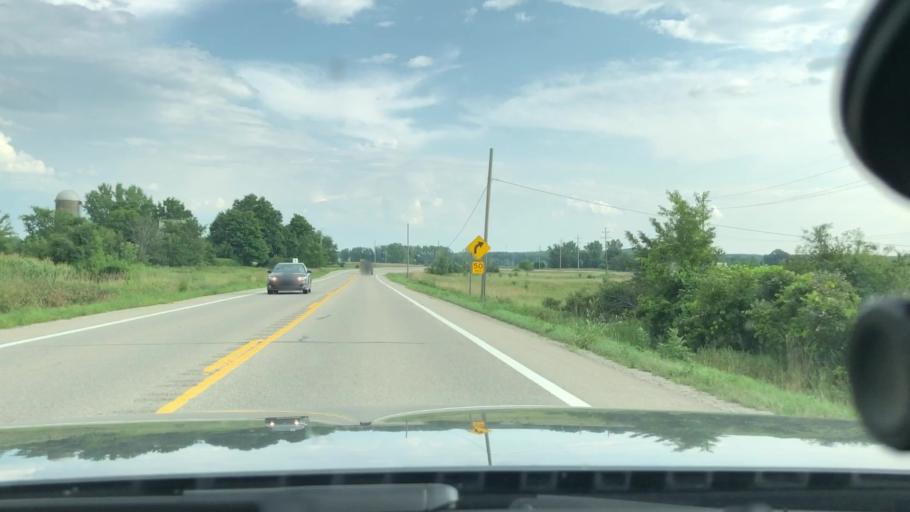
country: US
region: Michigan
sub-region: Washtenaw County
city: Chelsea
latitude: 42.2503
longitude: -84.0337
